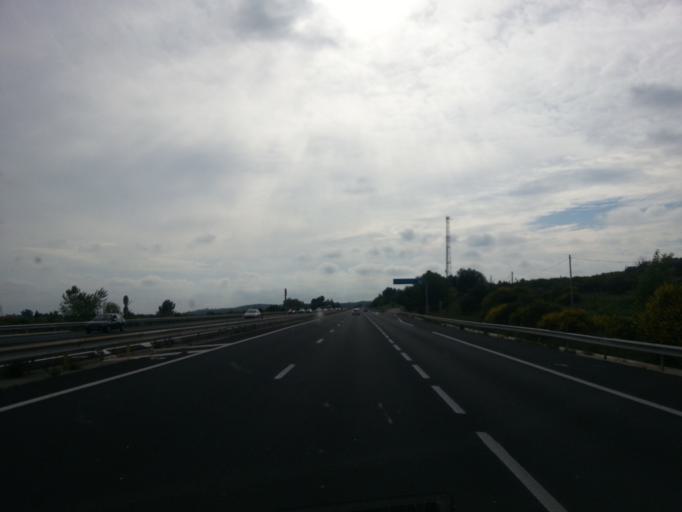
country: FR
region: Languedoc-Roussillon
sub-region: Departement du Gard
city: Sernhac
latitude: 43.9027
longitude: 4.5395
